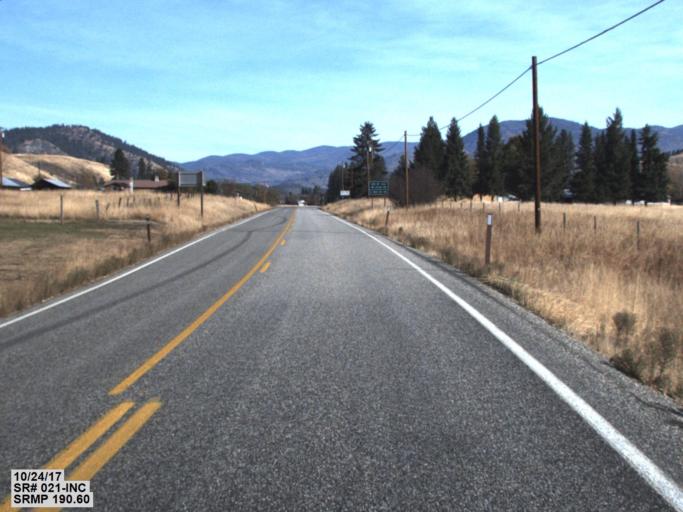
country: CA
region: British Columbia
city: Grand Forks
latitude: 48.9902
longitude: -118.5100
